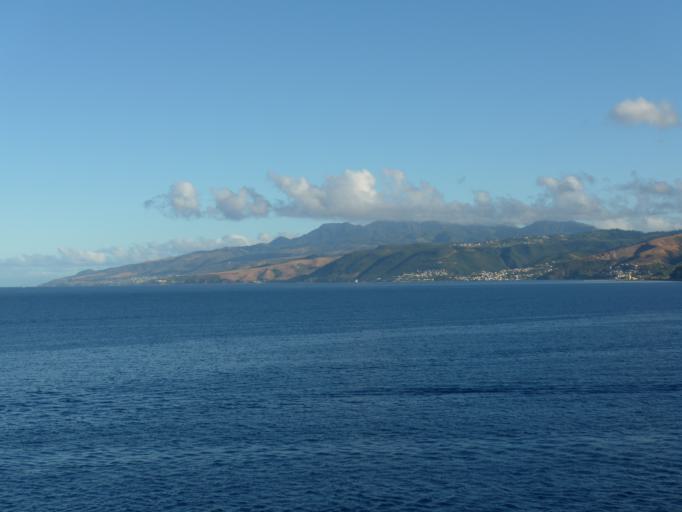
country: DM
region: Saint George
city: Roseau
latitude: 15.2961
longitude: -61.3972
